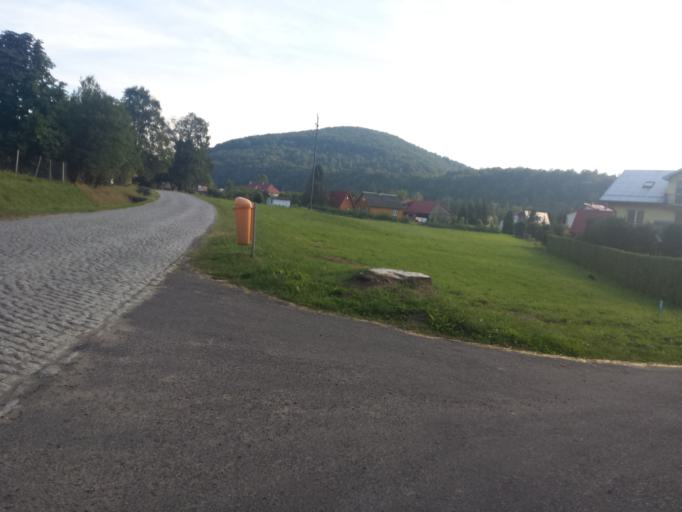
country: PL
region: Subcarpathian Voivodeship
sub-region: Powiat leski
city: Uherce Mineralne
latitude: 49.4386
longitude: 22.4104
